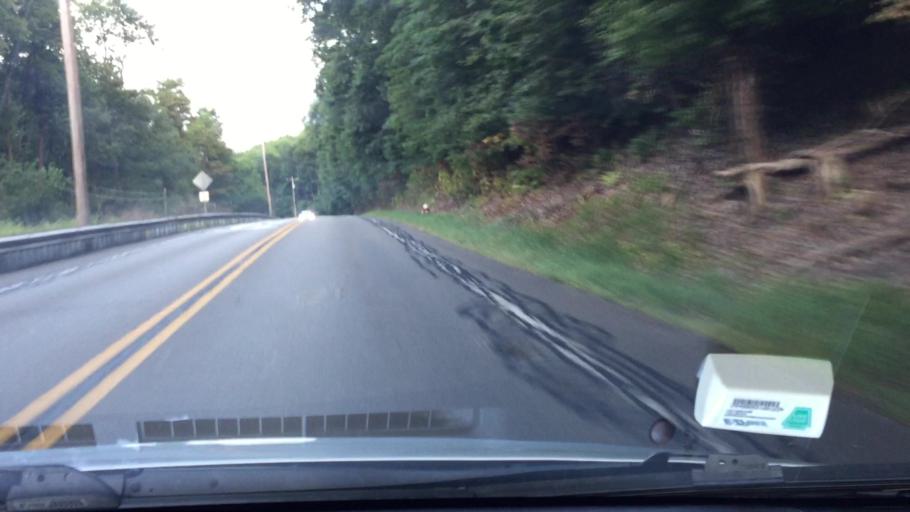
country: US
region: Pennsylvania
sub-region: Allegheny County
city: Gibsonia
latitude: 40.6327
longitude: -79.9944
